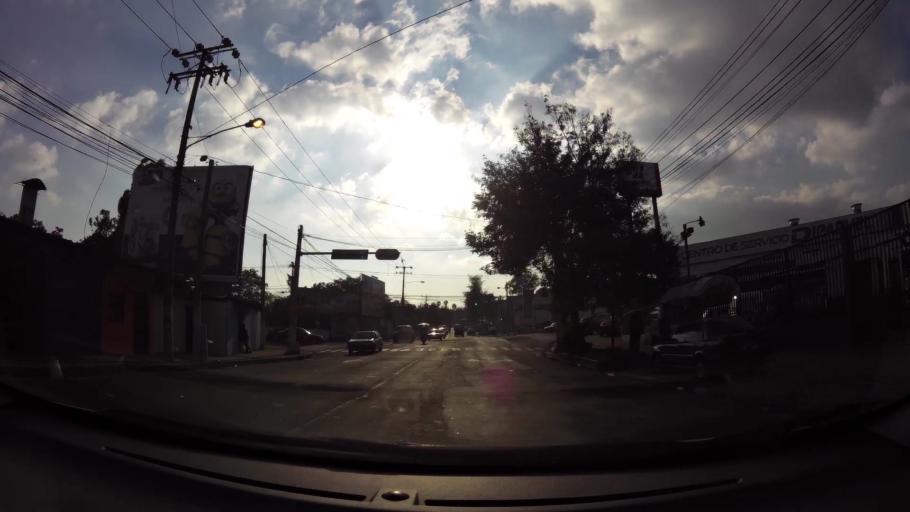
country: SV
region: La Libertad
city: Antiguo Cuscatlan
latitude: 13.6931
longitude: -89.2277
